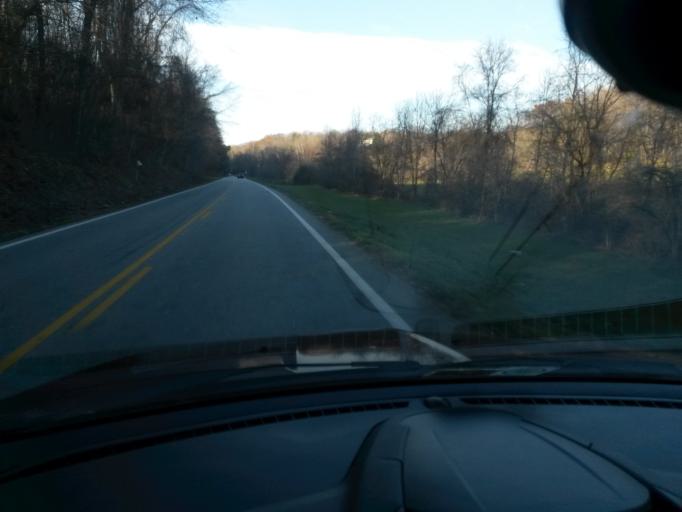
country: US
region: Virginia
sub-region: Amherst County
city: Amherst
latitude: 37.6322
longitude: -79.1178
